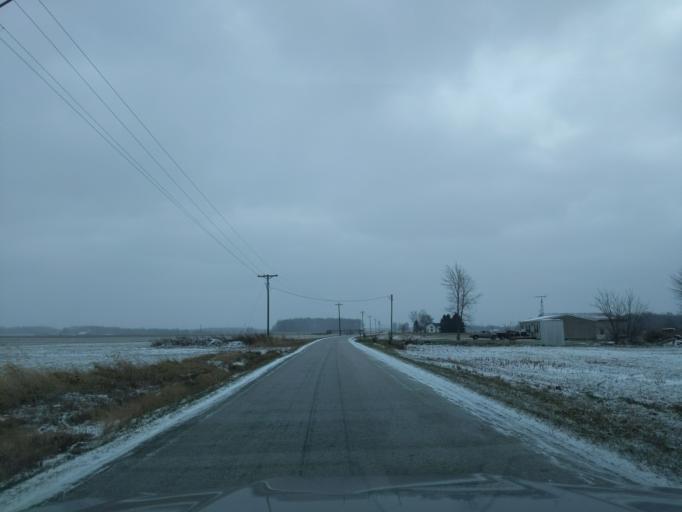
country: US
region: Indiana
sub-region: Decatur County
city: Greensburg
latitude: 39.2363
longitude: -85.4677
